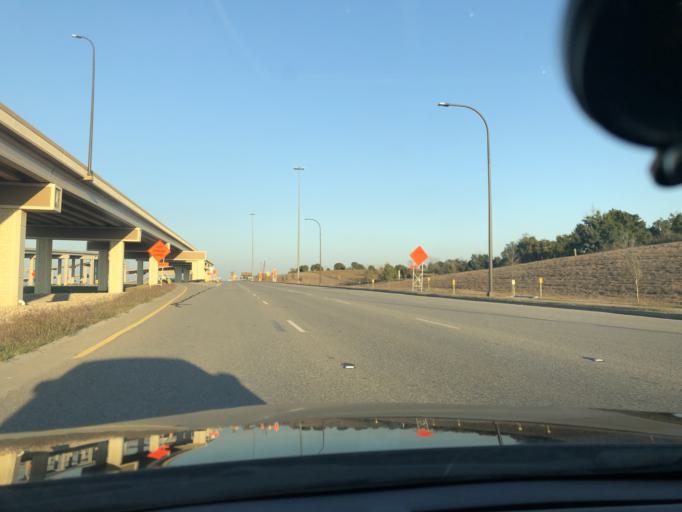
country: US
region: Texas
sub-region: Travis County
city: Manor
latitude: 30.3371
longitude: -97.5986
